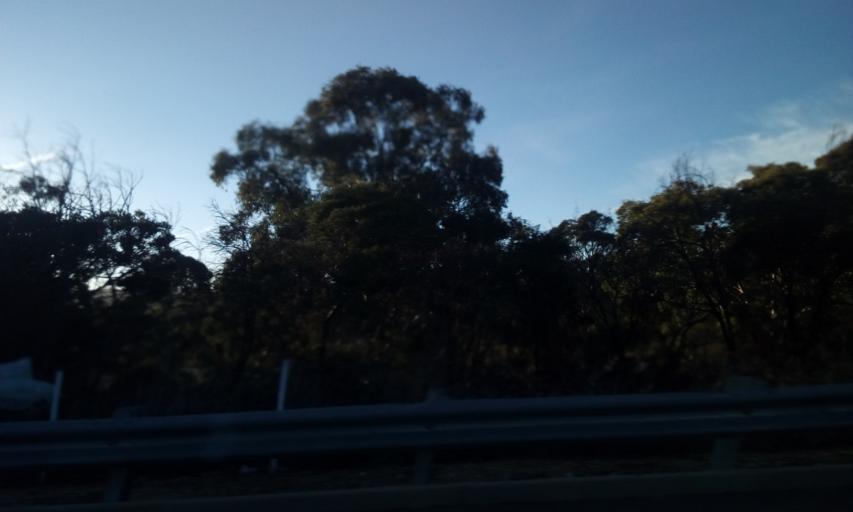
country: AU
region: New South Wales
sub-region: Yass Valley
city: Gundaroo
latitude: -35.1285
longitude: 149.3421
